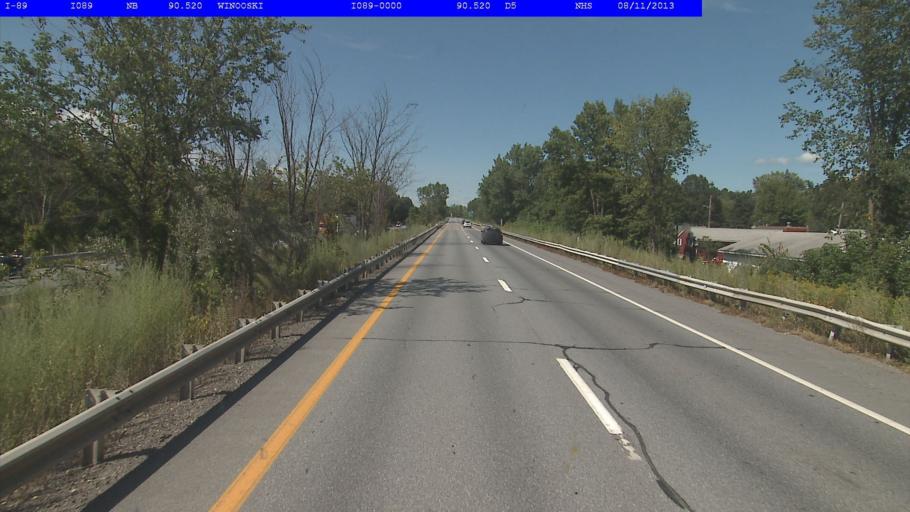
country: US
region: Vermont
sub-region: Chittenden County
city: Winooski
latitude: 44.4939
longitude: -73.1732
